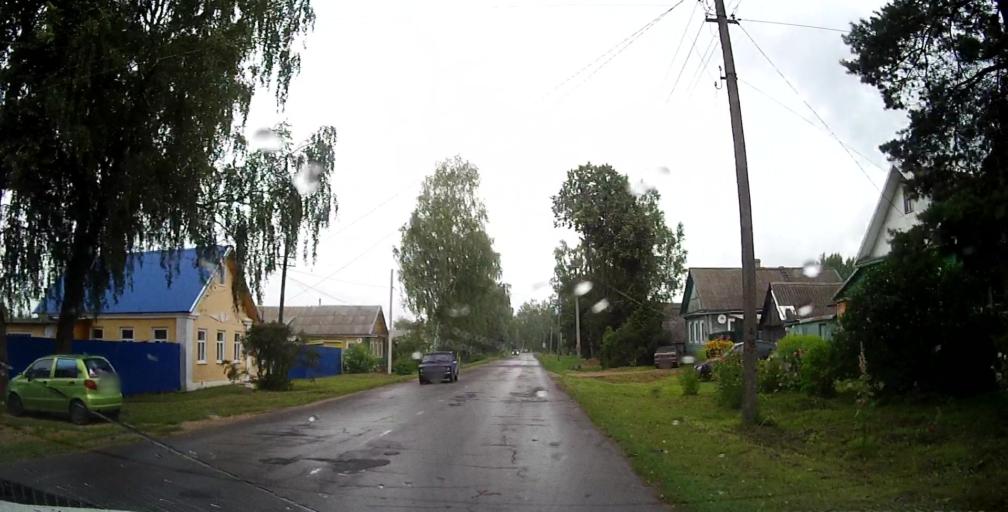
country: RU
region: Smolensk
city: Demidov
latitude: 55.2885
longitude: 31.5068
